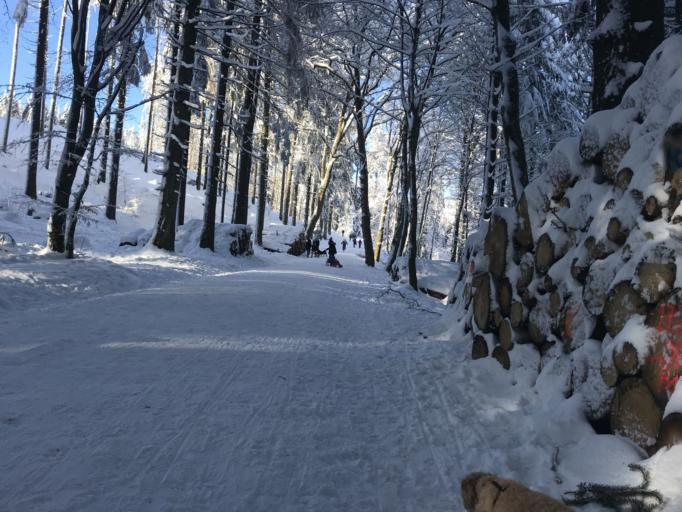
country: DE
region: Hesse
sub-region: Regierungsbezirk Darmstadt
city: Konigstein im Taunus
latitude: 50.2164
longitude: 8.4674
